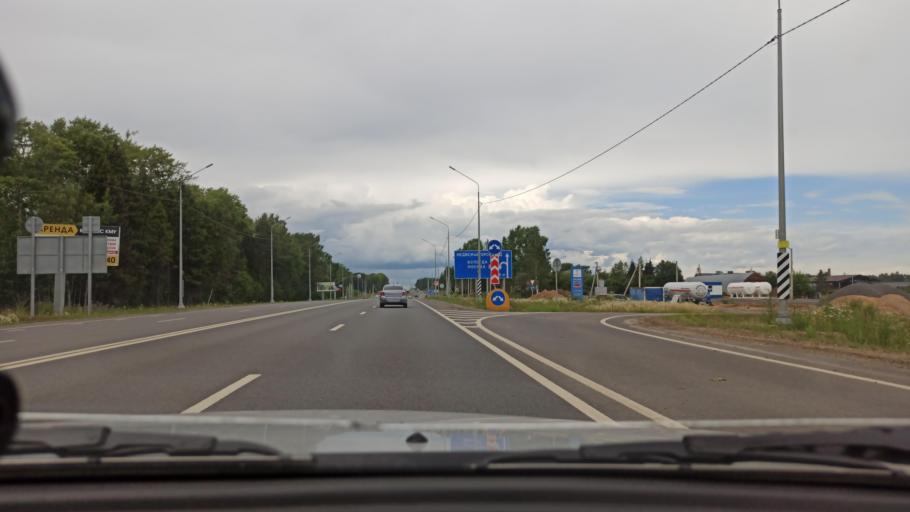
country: RU
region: Vologda
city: Molochnoye
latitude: 59.2532
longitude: 39.7642
